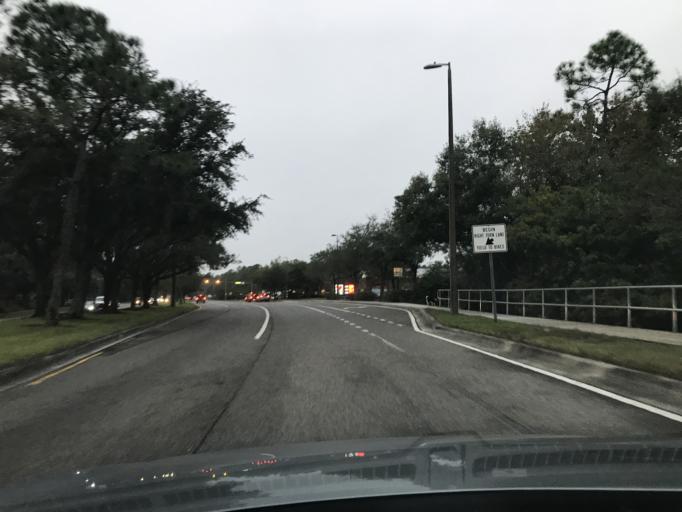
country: US
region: Florida
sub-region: Hillsborough County
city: Westchase
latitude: 28.0552
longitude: -82.6218
